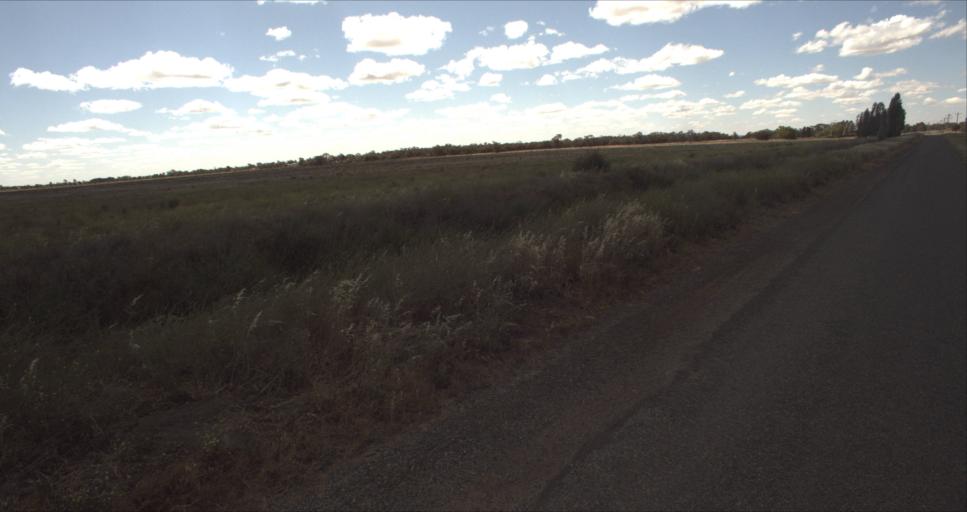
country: AU
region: New South Wales
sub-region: Leeton
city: Leeton
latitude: -34.5297
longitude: 146.2189
